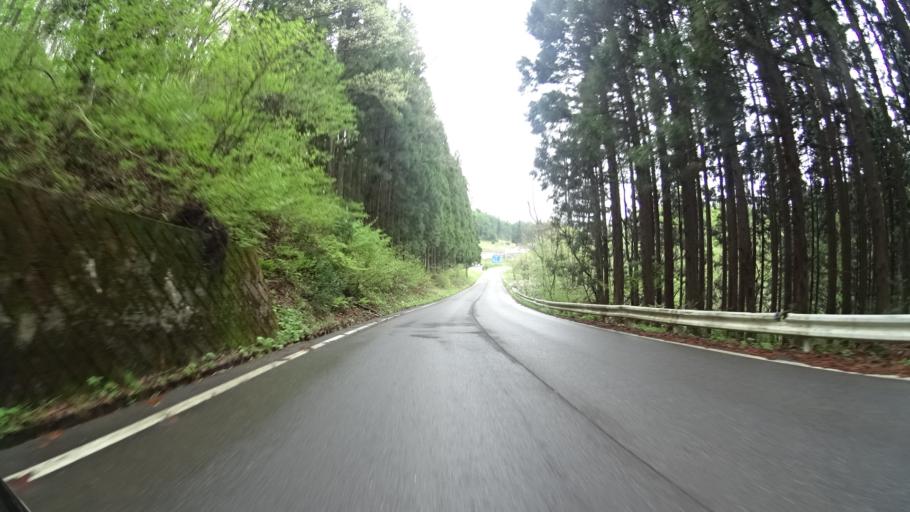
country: JP
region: Nagano
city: Nagano-shi
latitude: 36.7551
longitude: 138.1988
